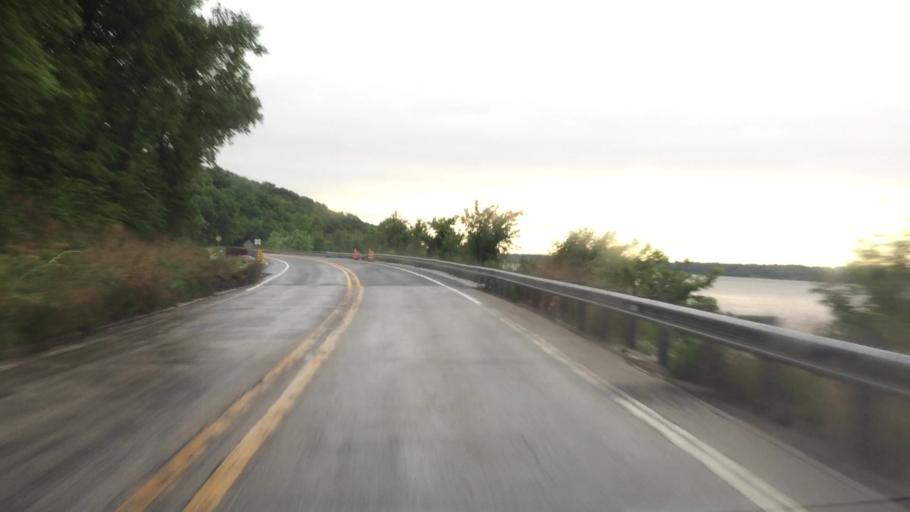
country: US
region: Iowa
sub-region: Lee County
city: Keokuk
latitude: 40.4673
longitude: -91.3622
